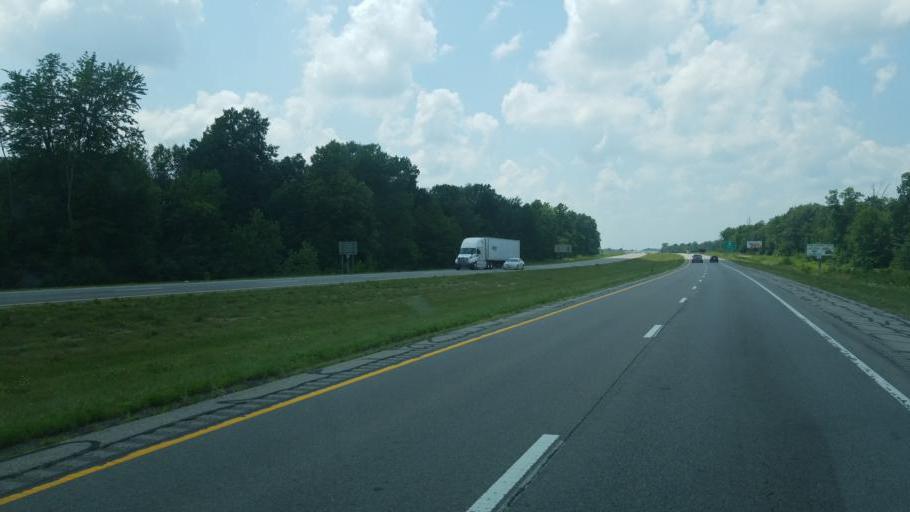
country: US
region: Ohio
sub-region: Crawford County
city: Crestline
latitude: 40.7627
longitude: -82.7258
